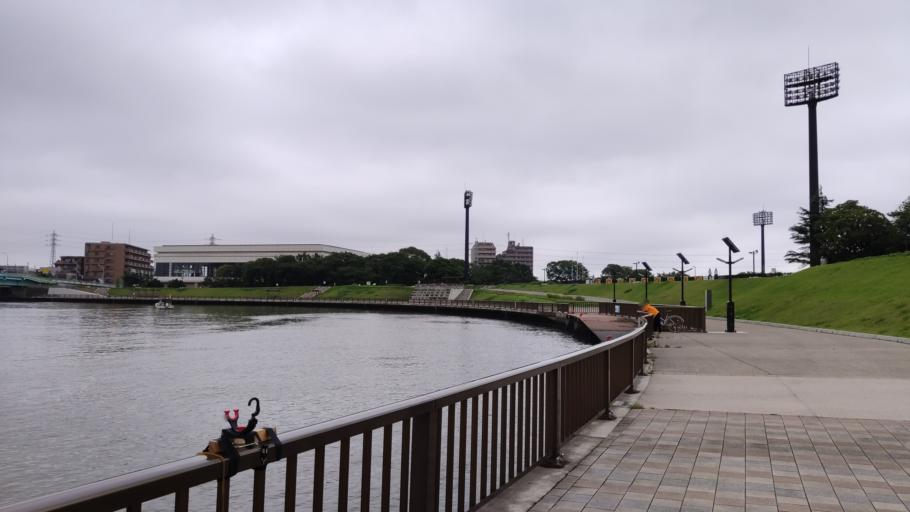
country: JP
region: Chiba
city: Matsudo
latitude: 35.7363
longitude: 139.8595
